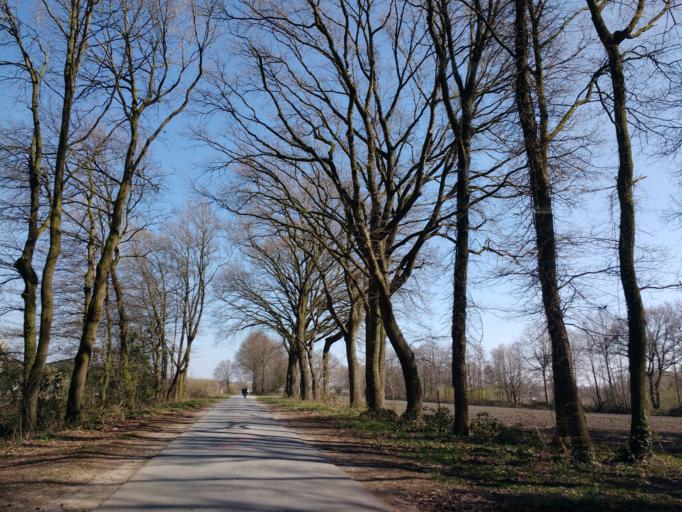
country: DE
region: North Rhine-Westphalia
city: Geseke
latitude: 51.7082
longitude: 8.4697
